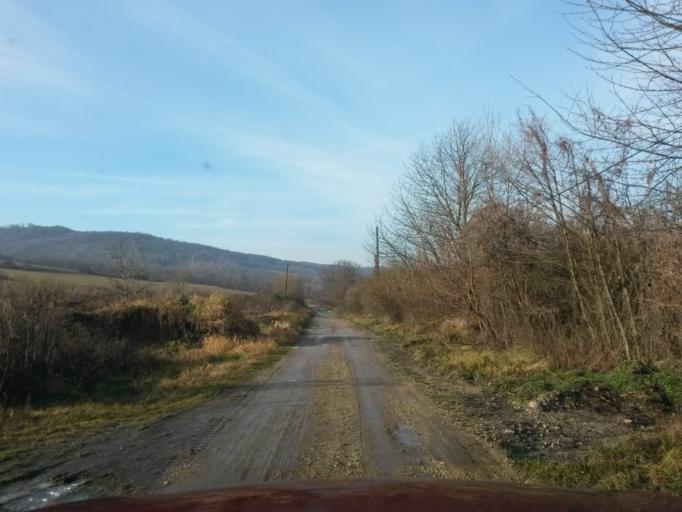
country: SK
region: Kosicky
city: Roznava
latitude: 48.7098
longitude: 20.4416
